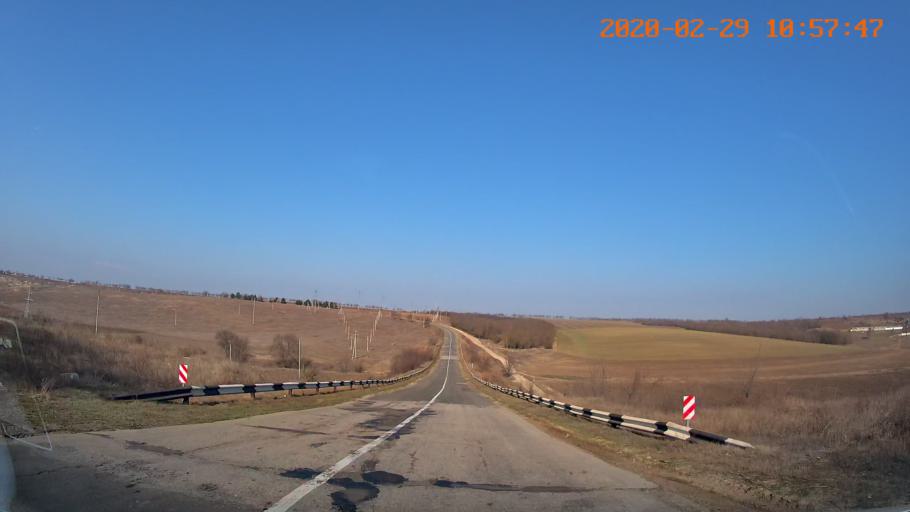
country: MD
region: Telenesti
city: Grigoriopol
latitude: 47.1633
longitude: 29.3206
